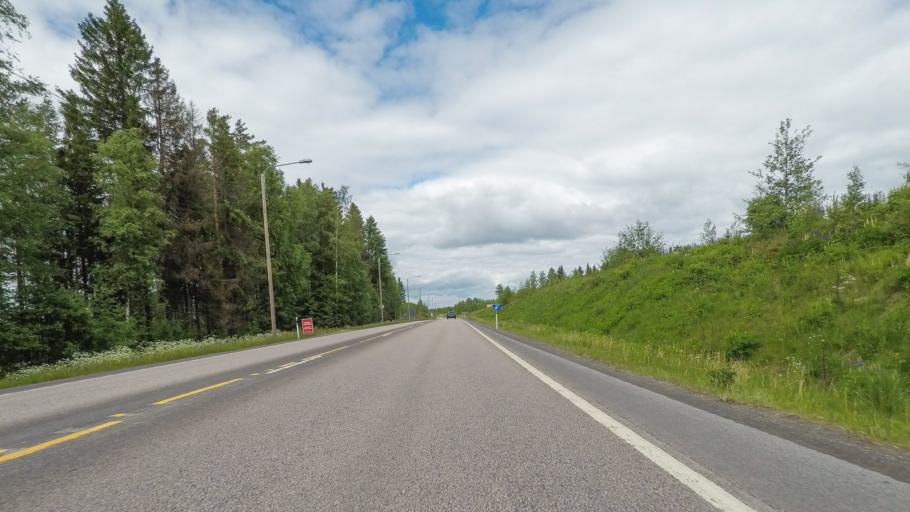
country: FI
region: Paijanne Tavastia
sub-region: Lahti
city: Hartola
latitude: 61.5805
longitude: 26.0079
